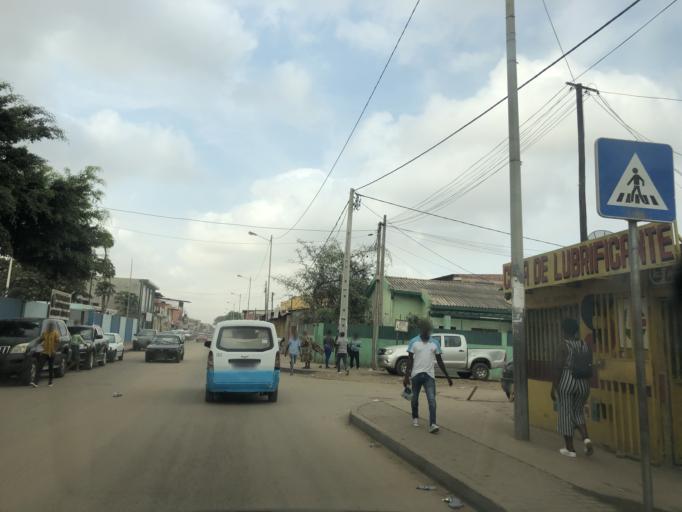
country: AO
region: Luanda
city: Luanda
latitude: -8.8397
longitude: 13.2629
